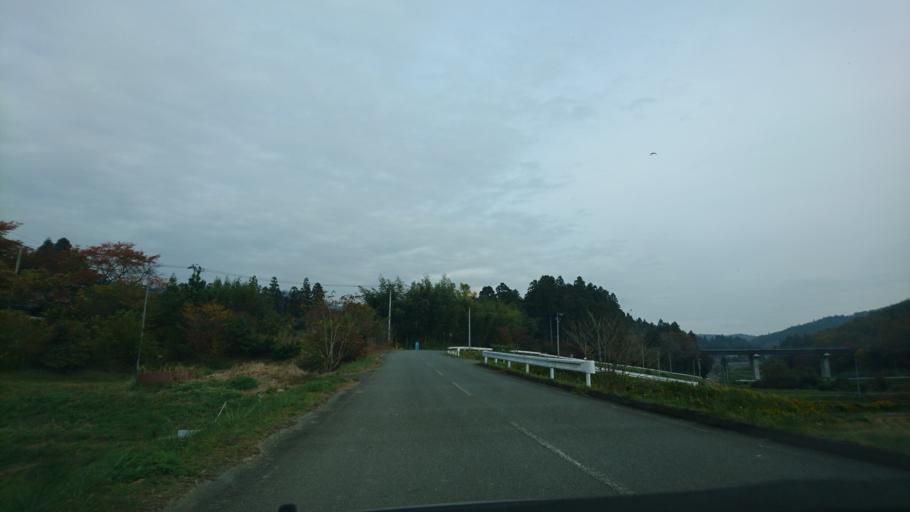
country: JP
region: Iwate
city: Ichinoseki
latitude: 38.9686
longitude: 141.1659
